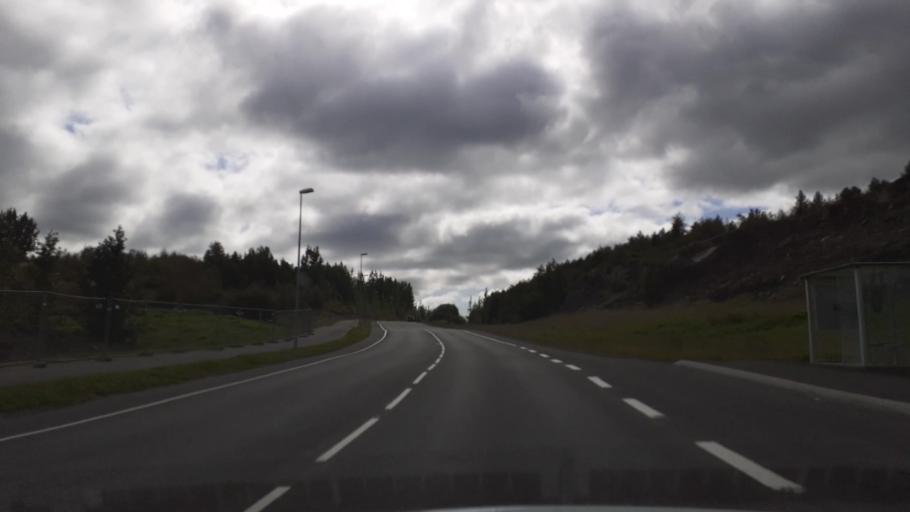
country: IS
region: Northeast
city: Akureyri
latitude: 65.6844
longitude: -18.1158
